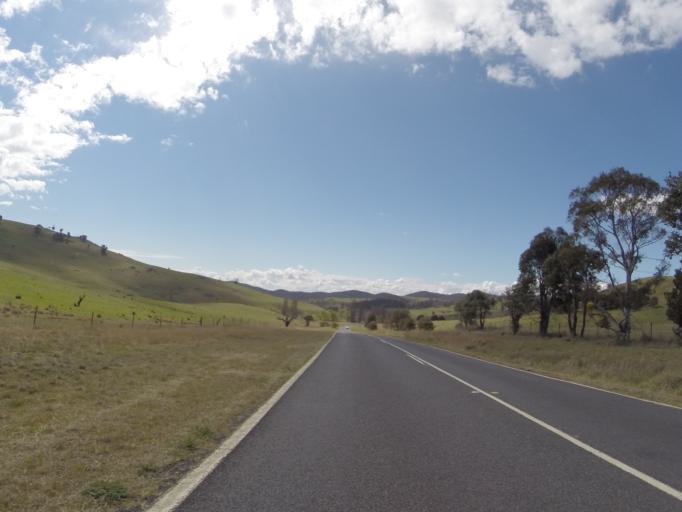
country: AU
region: Australian Capital Territory
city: Macarthur
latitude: -35.4056
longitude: 148.9559
